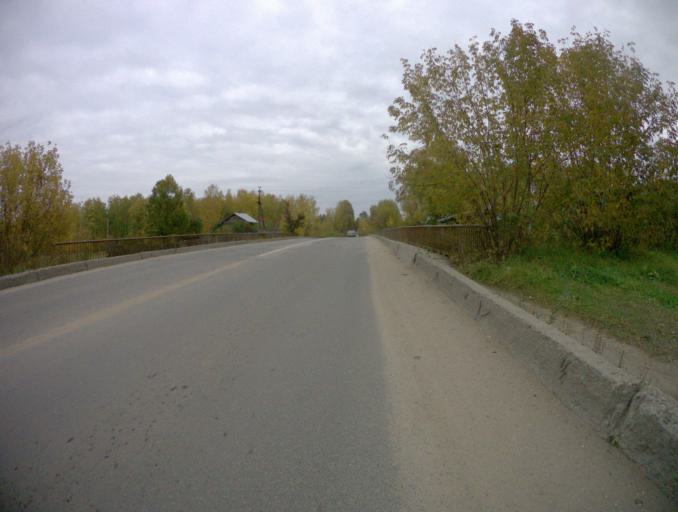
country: RU
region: Vladimir
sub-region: Kovrovskiy Rayon
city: Kovrov
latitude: 56.3716
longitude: 41.3417
